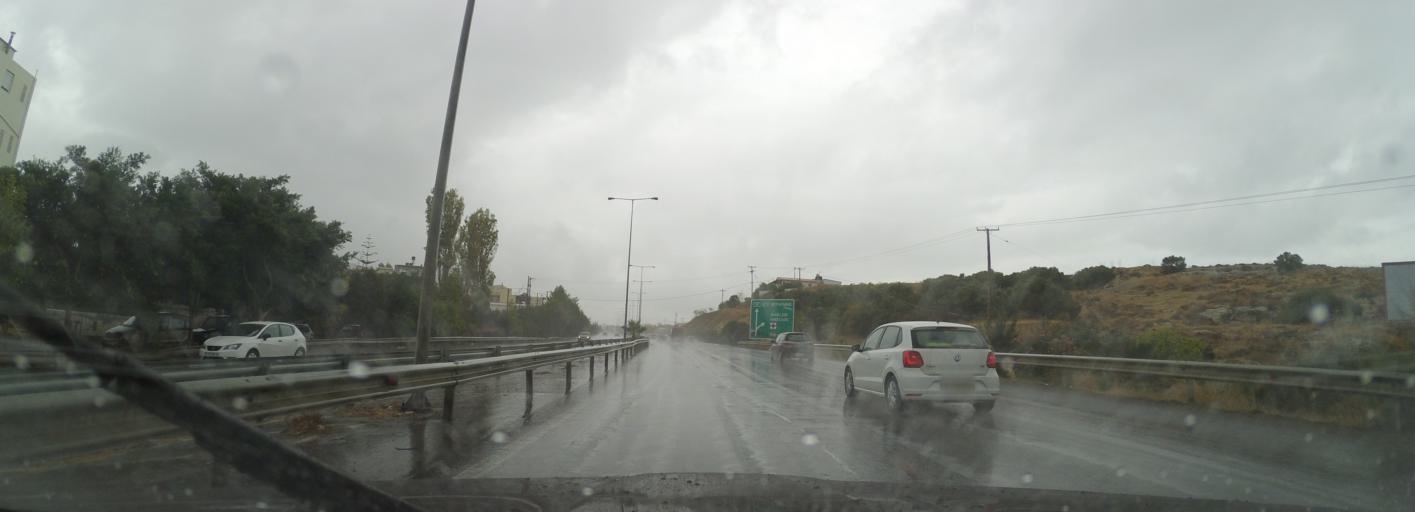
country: GR
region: Crete
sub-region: Nomos Irakleiou
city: Irakleion
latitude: 35.3283
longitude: 25.1526
